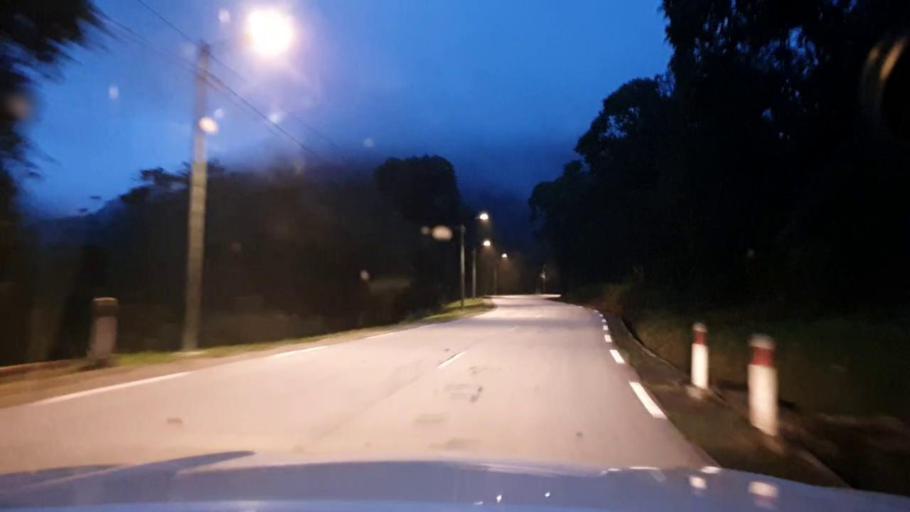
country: RW
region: Southern Province
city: Nzega
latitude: -2.5309
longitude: 29.3929
